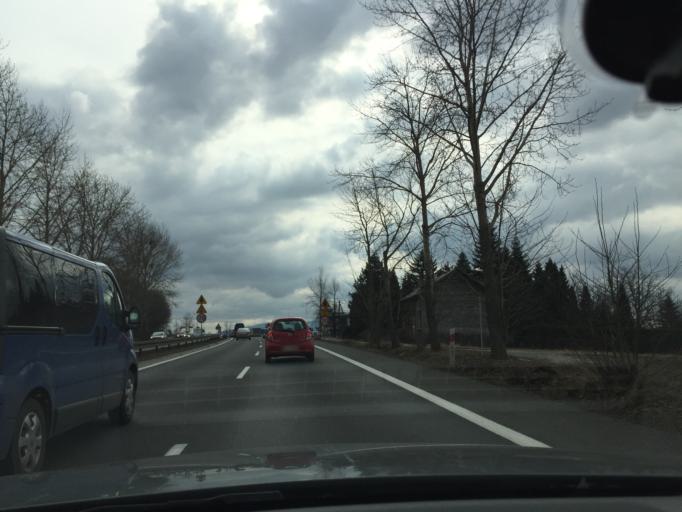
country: PL
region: Silesian Voivodeship
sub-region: Powiat bielski
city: Czechowice-Dziedzice
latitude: 49.8952
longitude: 18.9924
